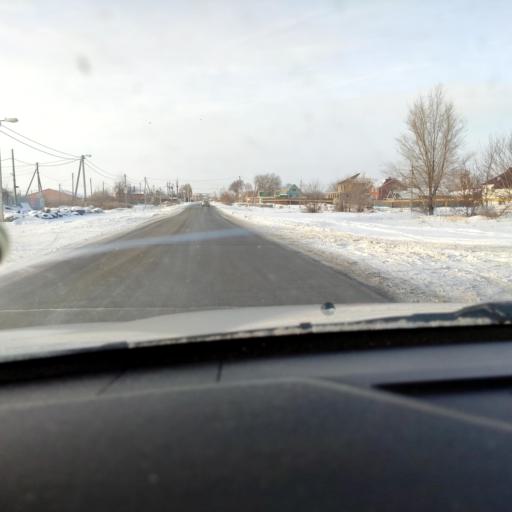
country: RU
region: Samara
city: Smyshlyayevka
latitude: 53.1598
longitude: 50.3854
